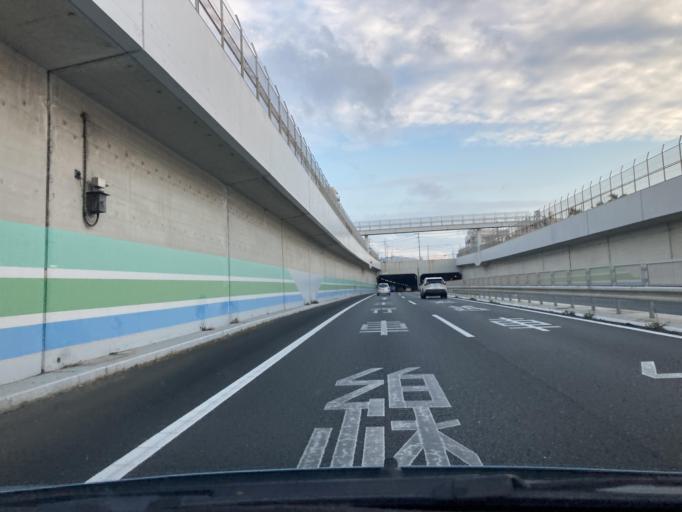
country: JP
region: Okinawa
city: Okinawa
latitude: 26.3246
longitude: 127.7879
